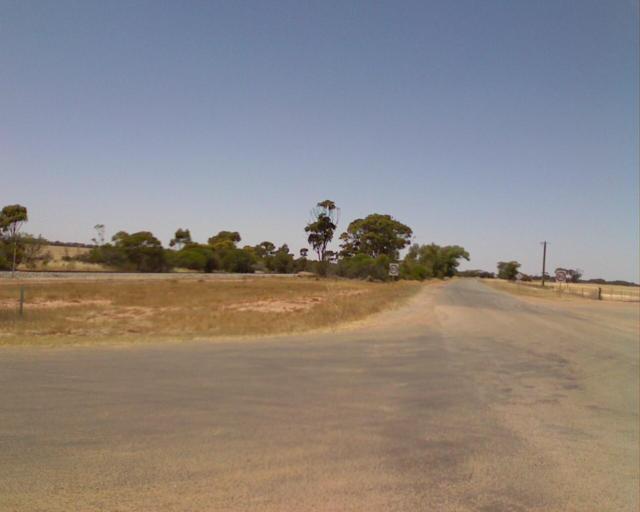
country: AU
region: Western Australia
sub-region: Wongan-Ballidu
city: Wongan Hills
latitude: -30.3669
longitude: 117.1211
